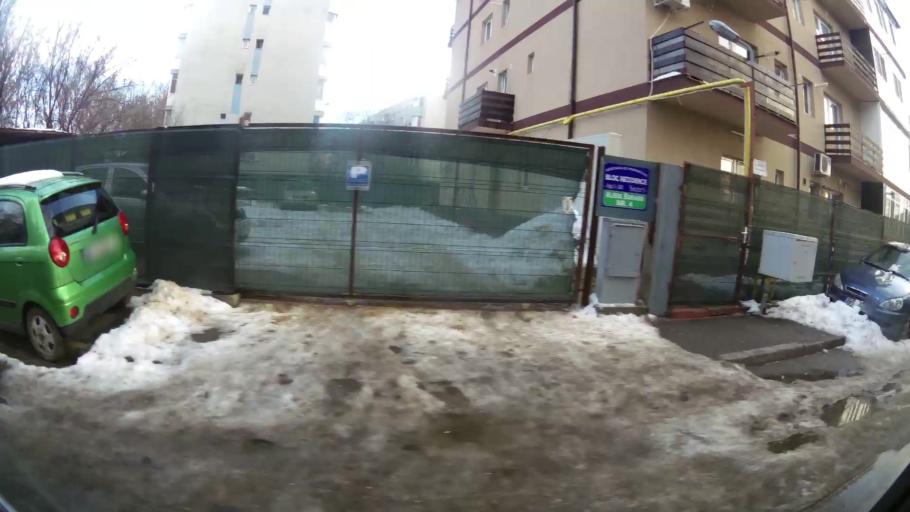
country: RO
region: Bucuresti
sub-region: Municipiul Bucuresti
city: Bucuresti
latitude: 44.3899
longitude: 26.0747
